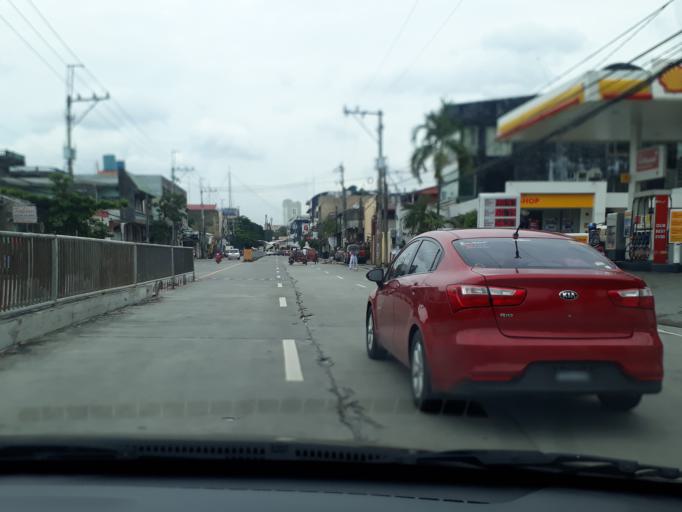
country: PH
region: Metro Manila
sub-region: Mandaluyong
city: Mandaluyong City
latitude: 14.5750
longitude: 121.0314
